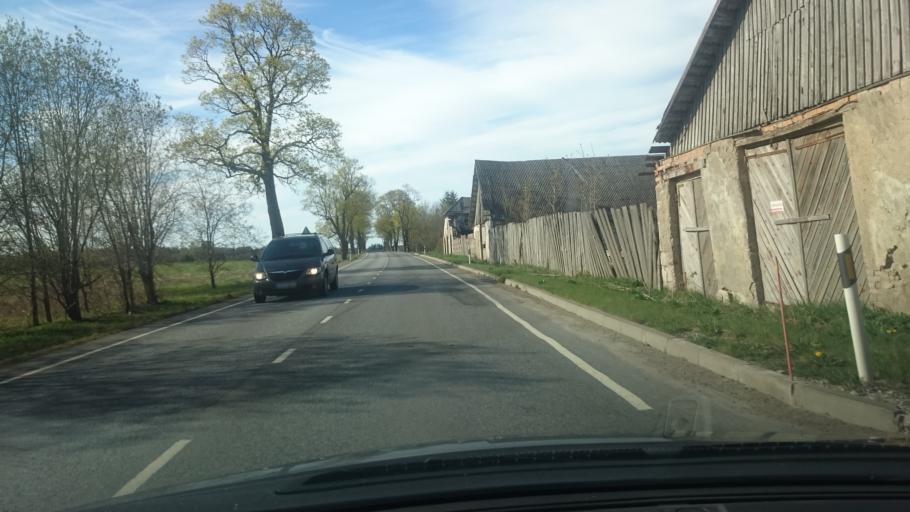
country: EE
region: Ida-Virumaa
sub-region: Johvi vald
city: Johvi
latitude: 59.2728
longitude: 27.5117
